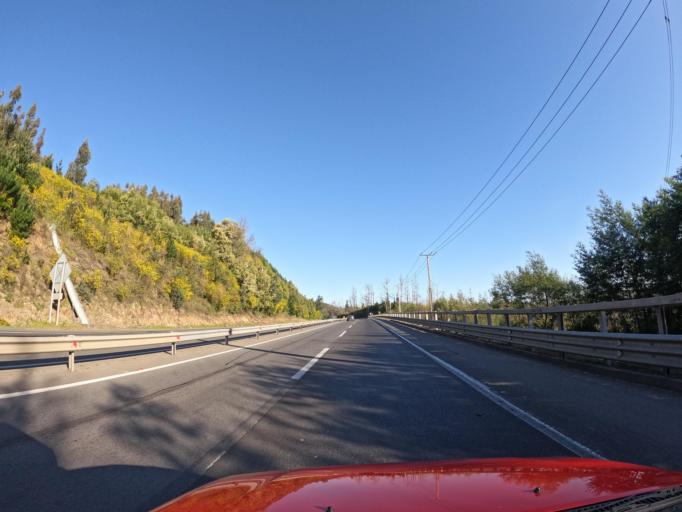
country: CL
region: Biobio
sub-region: Provincia de Concepcion
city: Penco
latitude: -36.7559
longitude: -72.9782
